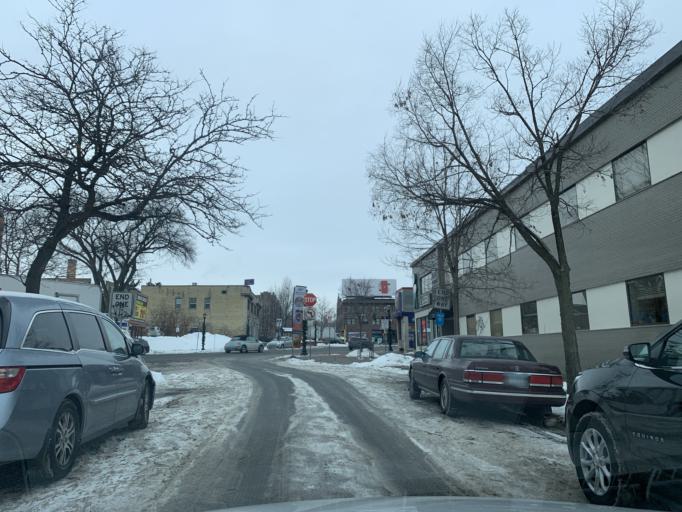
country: US
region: Minnesota
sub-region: Hennepin County
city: Minneapolis
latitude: 44.9616
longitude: -93.2918
